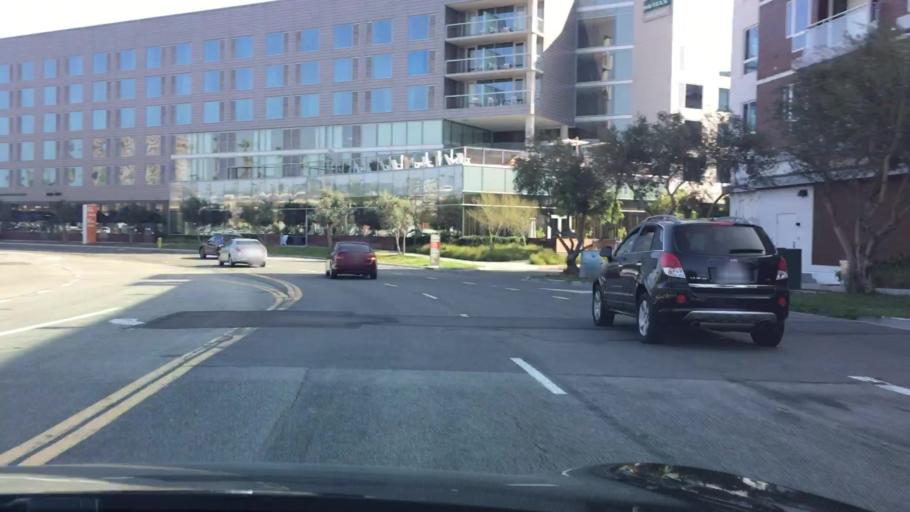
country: US
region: California
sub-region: Orange County
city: Irvine
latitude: 33.6714
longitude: -117.8447
